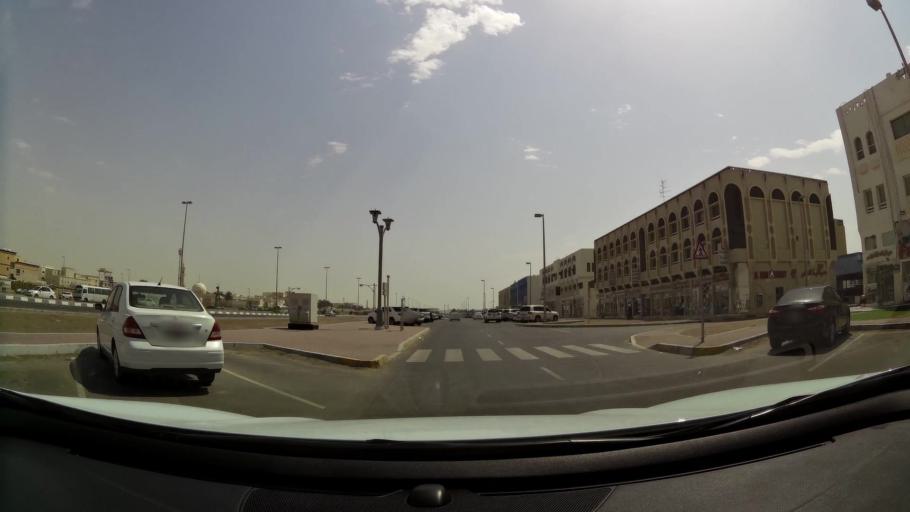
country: AE
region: Abu Dhabi
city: Abu Dhabi
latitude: 24.2971
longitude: 54.6387
